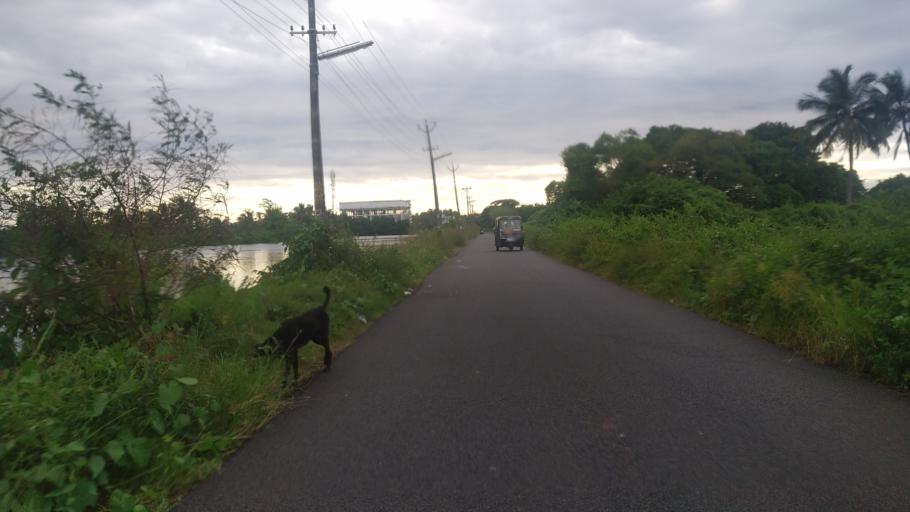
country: IN
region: Kerala
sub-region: Alappuzha
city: Arukutti
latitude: 9.8574
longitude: 76.2743
